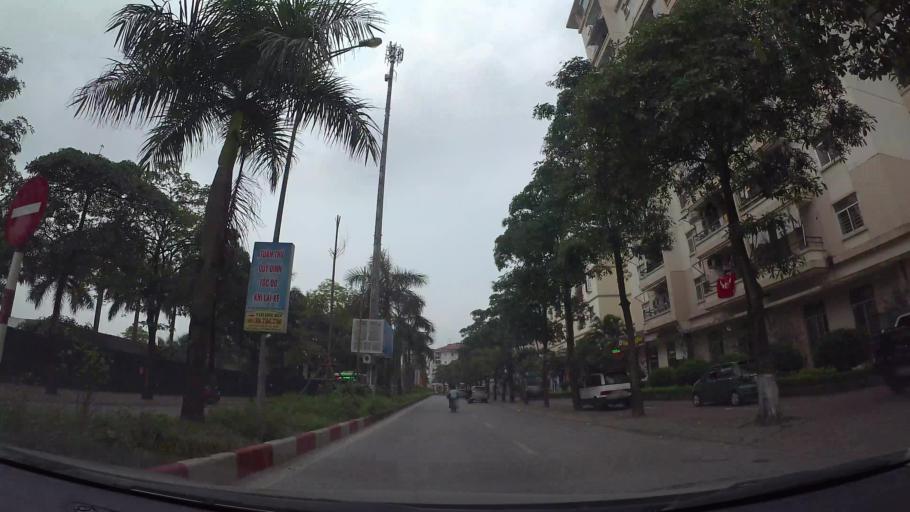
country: VN
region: Ha Noi
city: Trau Quy
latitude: 21.0640
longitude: 105.9082
